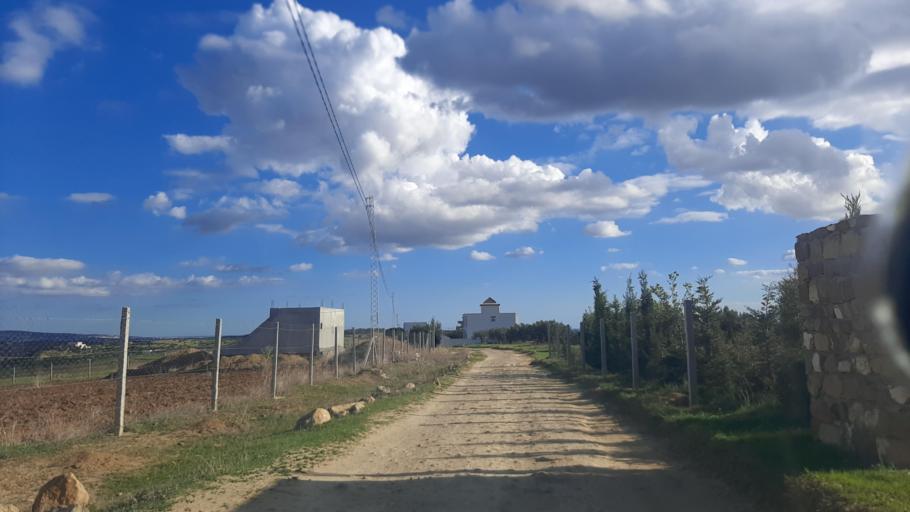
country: TN
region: Nabul
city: Bu `Urqub
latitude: 36.4667
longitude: 10.4804
